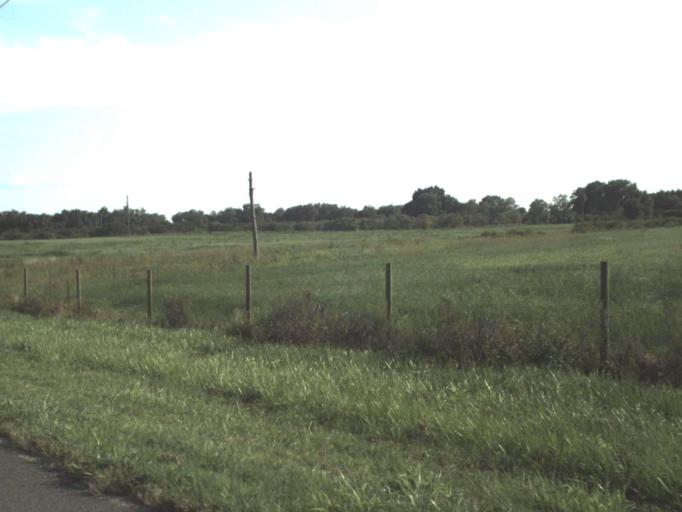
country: US
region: Florida
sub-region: Lake County
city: Groveland
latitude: 28.4801
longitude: -81.8356
